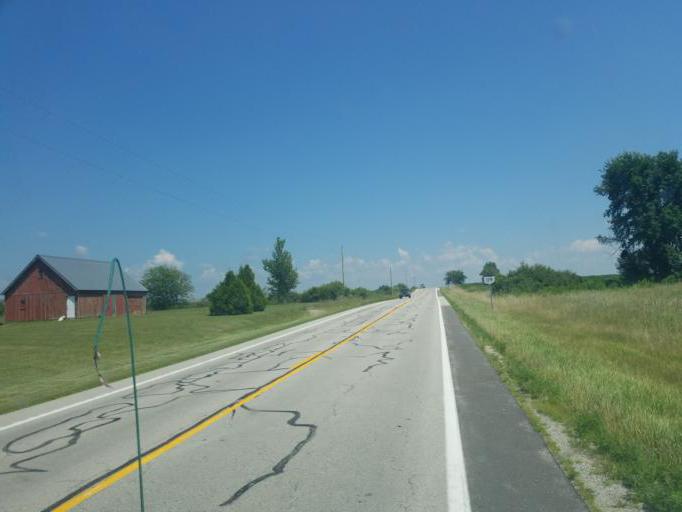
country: US
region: Ohio
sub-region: Shelby County
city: Jackson Center
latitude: 40.3958
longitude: -84.0927
